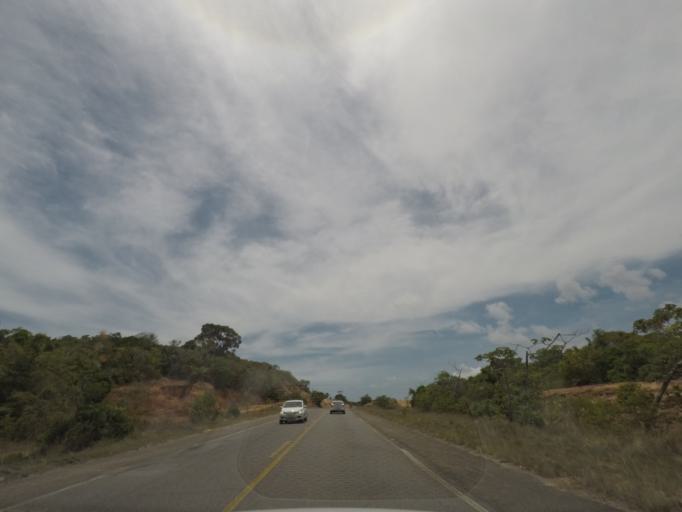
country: BR
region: Bahia
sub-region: Conde
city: Conde
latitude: -12.0195
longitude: -37.6909
